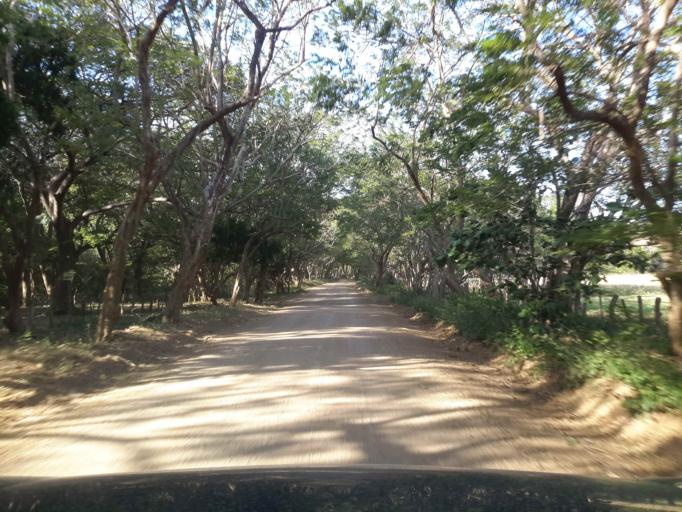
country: NI
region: Rivas
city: San Juan del Sur
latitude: 11.1943
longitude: -85.8112
